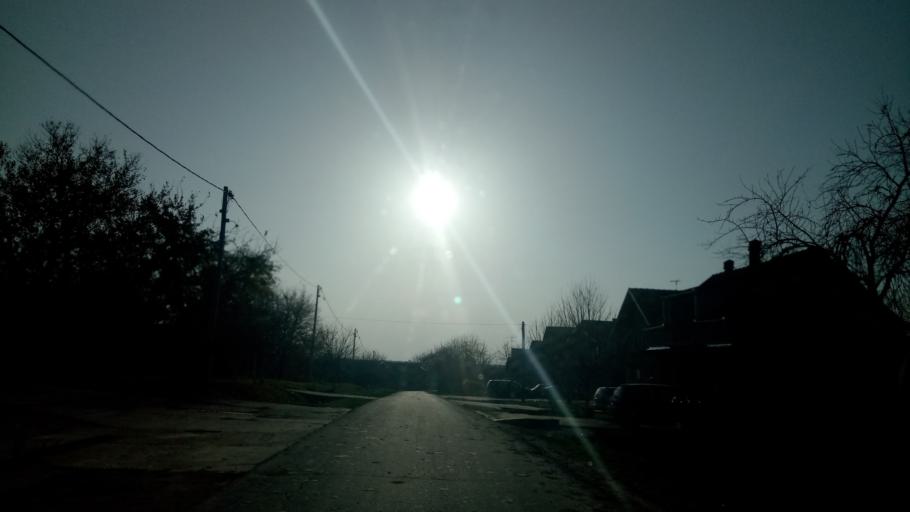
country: RS
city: Novi Slankamen
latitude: 45.1305
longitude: 20.2319
